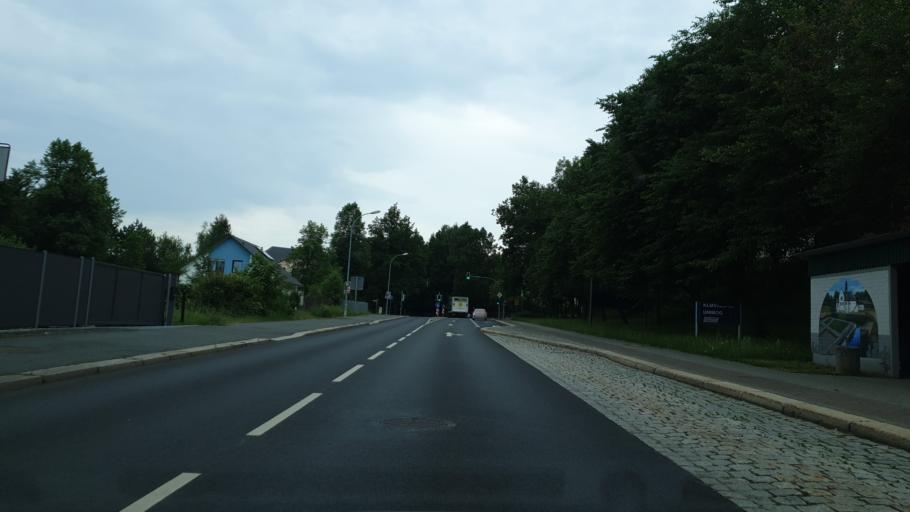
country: DE
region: Saxony
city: Auerbach
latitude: 50.5251
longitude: 12.3995
